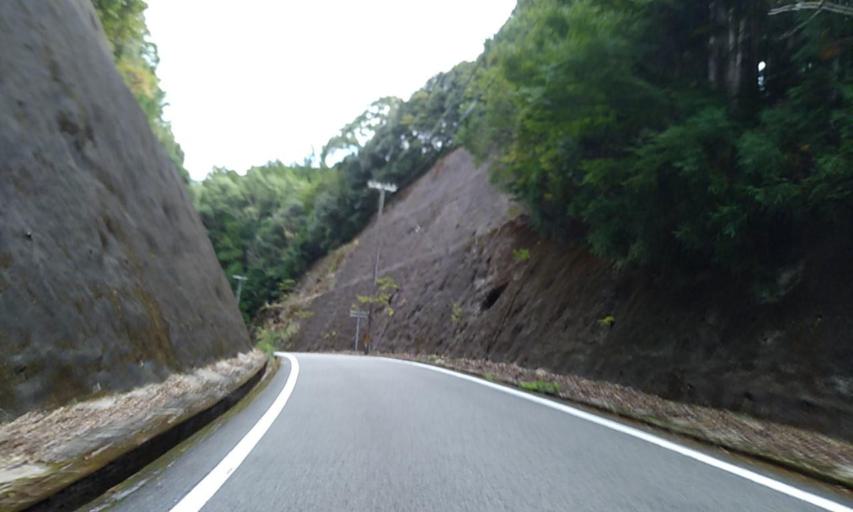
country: JP
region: Wakayama
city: Shingu
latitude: 33.5406
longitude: 135.8360
